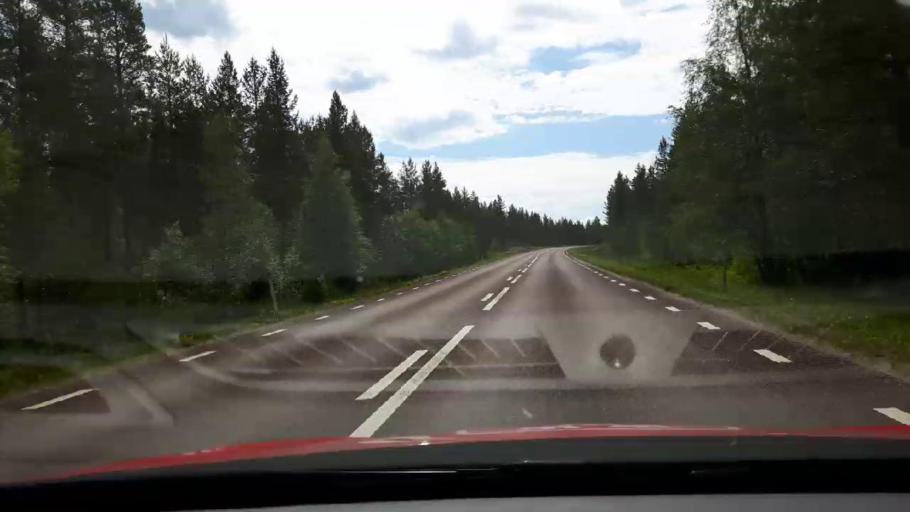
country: SE
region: Jaemtland
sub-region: Harjedalens Kommun
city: Sveg
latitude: 62.1080
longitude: 14.9710
